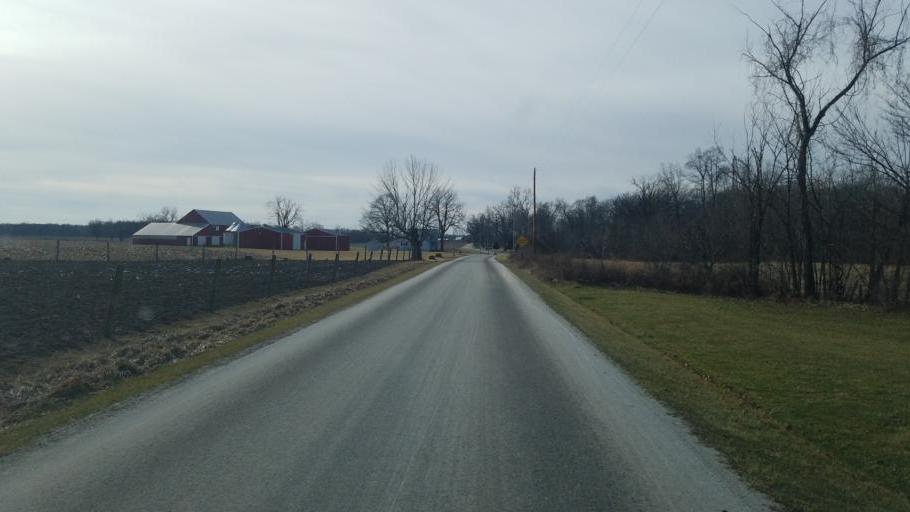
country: US
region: Ohio
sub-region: Hardin County
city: Kenton
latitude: 40.6097
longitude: -83.5101
